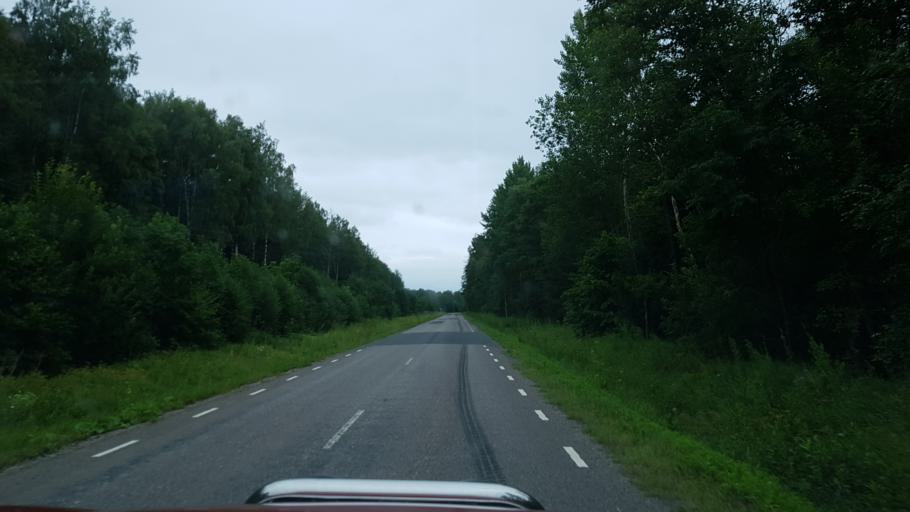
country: EE
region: Ida-Virumaa
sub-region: Johvi vald
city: Johvi
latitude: 59.4209
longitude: 27.4065
